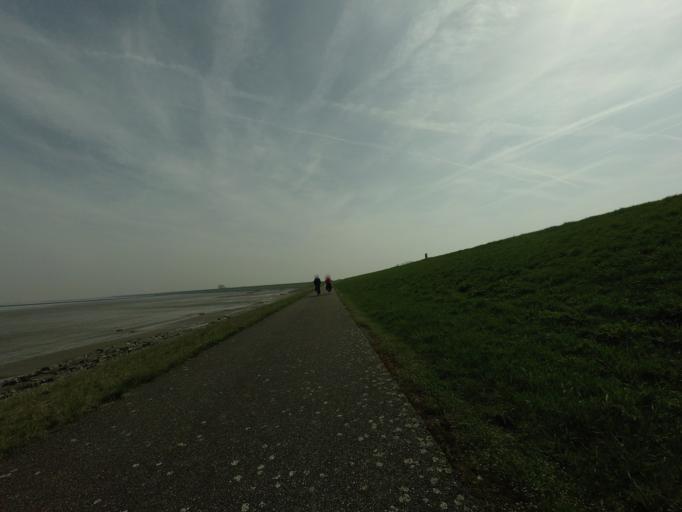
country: NL
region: Zeeland
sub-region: Gemeente Hulst
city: Hulst
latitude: 51.3690
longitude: 4.0463
